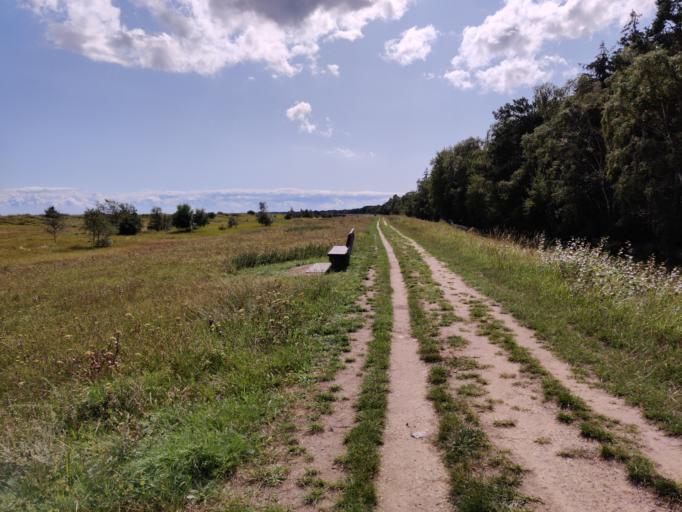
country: DK
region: Zealand
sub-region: Guldborgsund Kommune
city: Nykobing Falster
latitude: 54.6842
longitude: 11.9662
